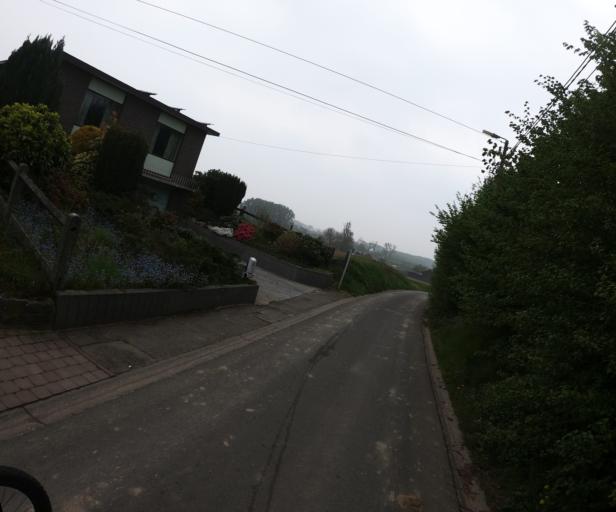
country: BE
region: Flanders
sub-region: Provincie Vlaams-Brabant
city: Pepingen
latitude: 50.7302
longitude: 4.1567
